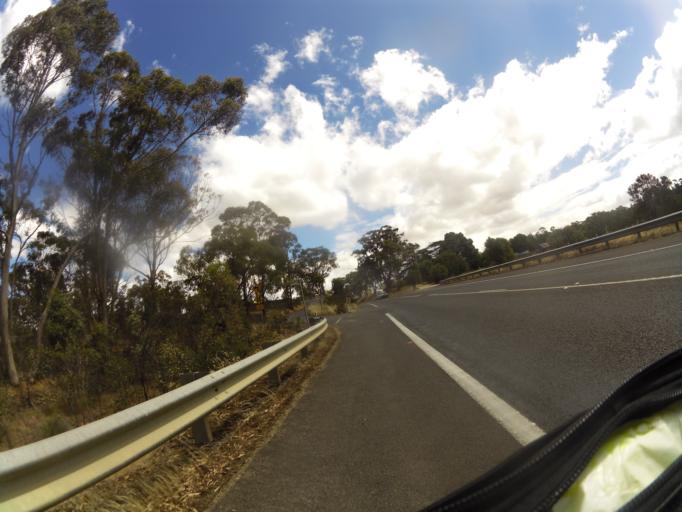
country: AU
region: Victoria
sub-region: Mount Alexander
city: Castlemaine
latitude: -37.0370
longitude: 144.2282
